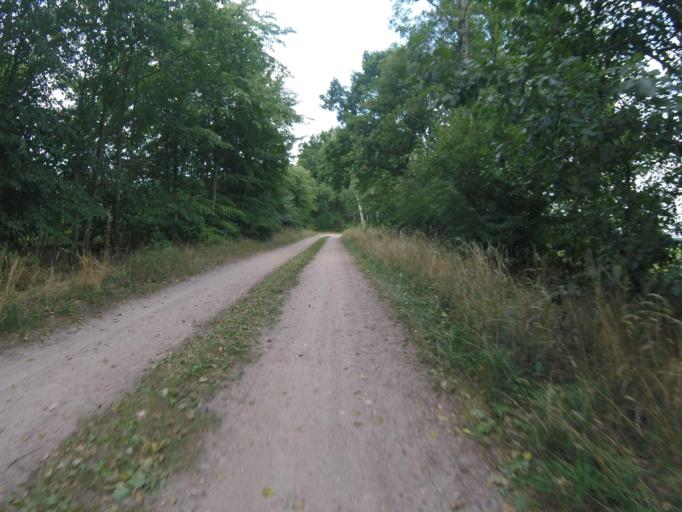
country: DE
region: Brandenburg
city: Spreenhagen
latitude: 52.2953
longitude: 13.8007
